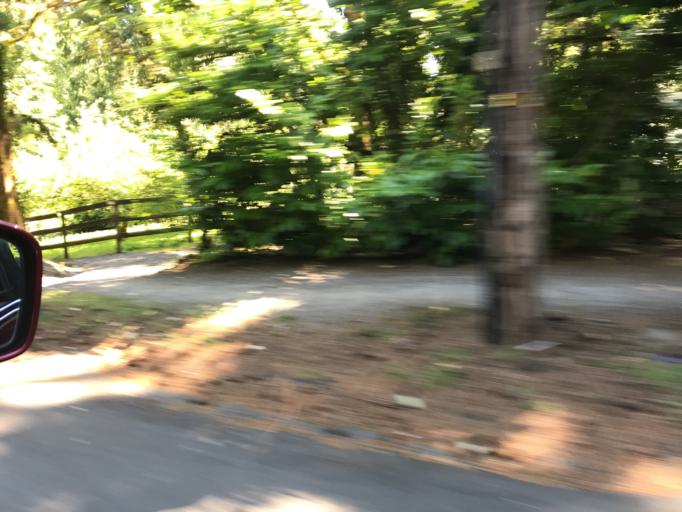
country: US
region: Washington
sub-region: King County
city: Bellevue
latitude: 47.6404
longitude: -122.1621
